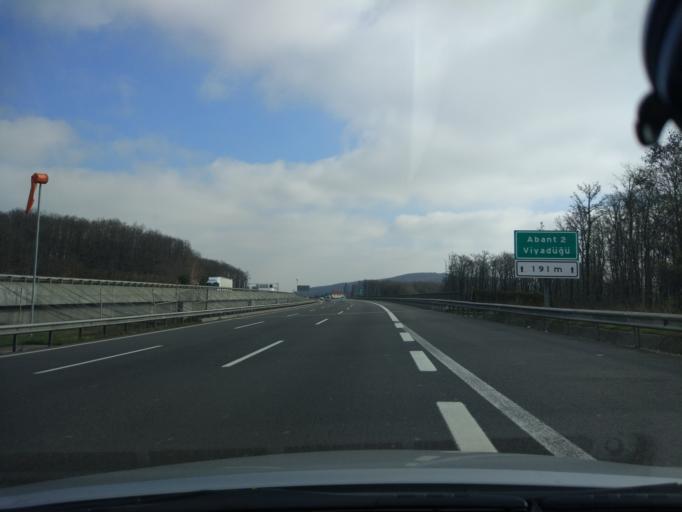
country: TR
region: Bolu
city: Bolu
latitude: 40.7206
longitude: 31.4863
